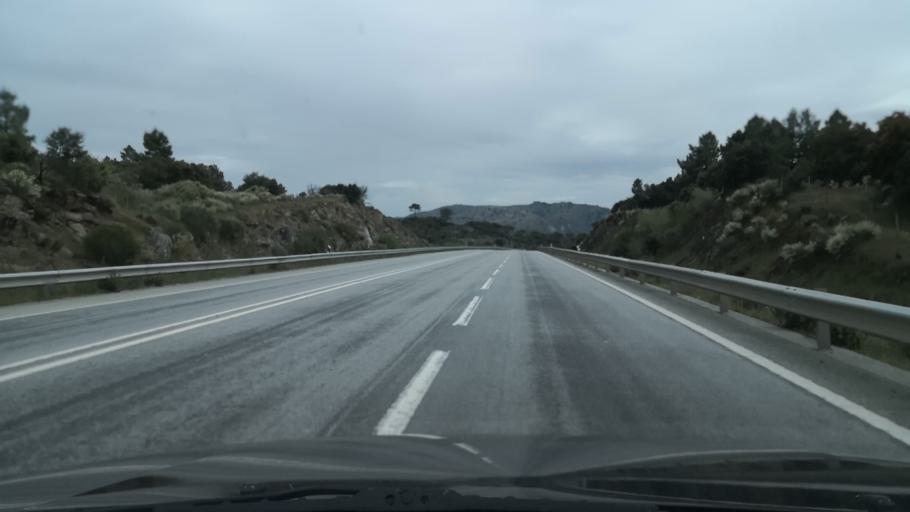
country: PT
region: Guarda
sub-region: Celorico da Beira
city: Celorico da Beira
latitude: 40.6314
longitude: -7.3116
